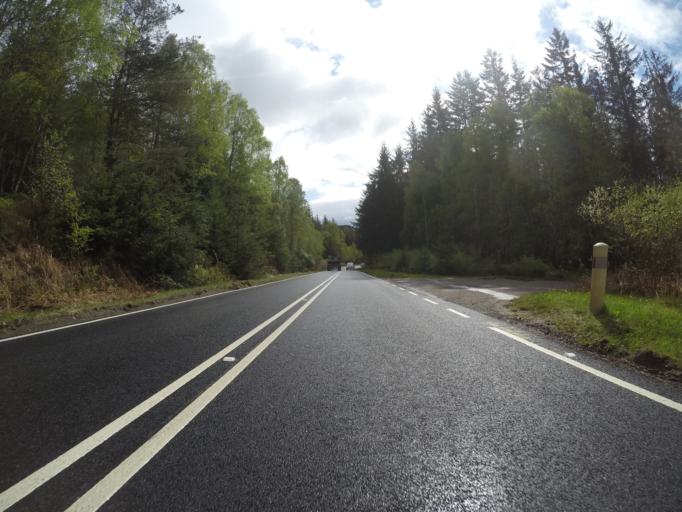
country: GB
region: Scotland
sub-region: Highland
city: Spean Bridge
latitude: 57.0751
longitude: -4.8379
